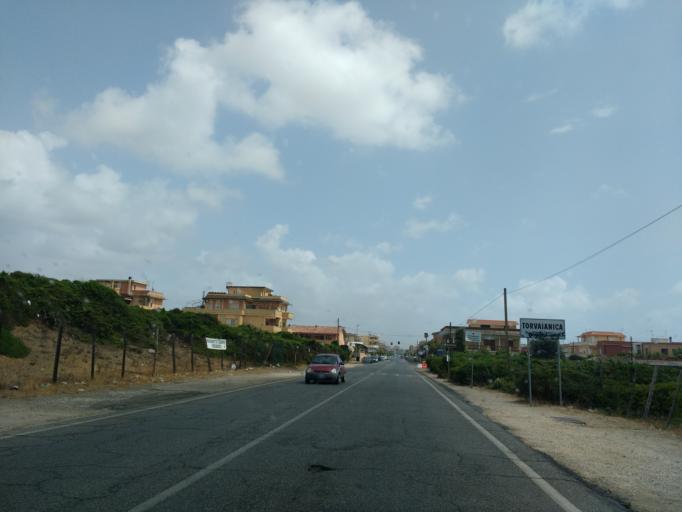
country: IT
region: Latium
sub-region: Citta metropolitana di Roma Capitale
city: Torvaianica
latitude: 41.6488
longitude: 12.4277
